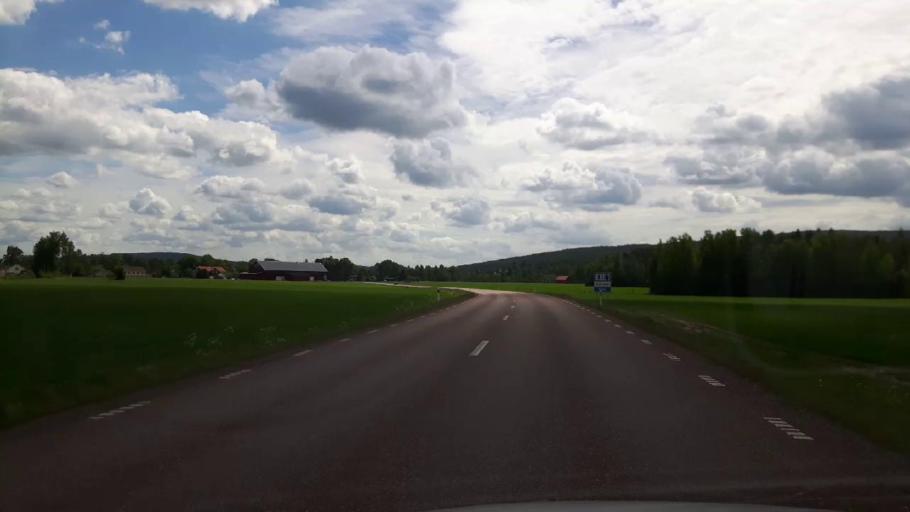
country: SE
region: Dalarna
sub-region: Saters Kommun
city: Saeter
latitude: 60.4018
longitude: 15.8746
